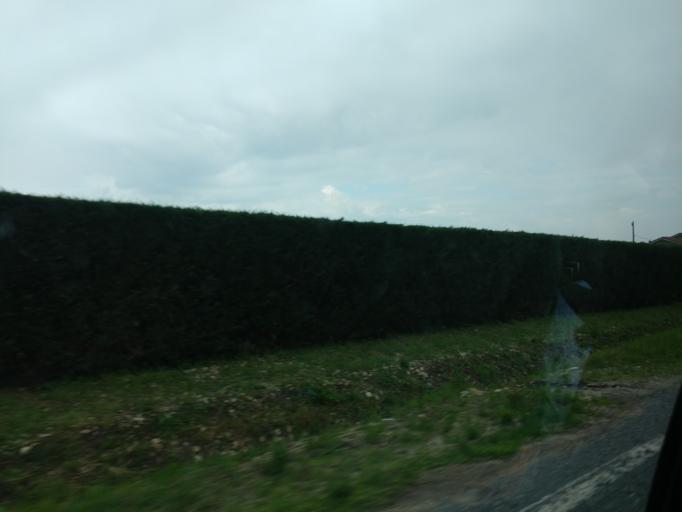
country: IT
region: Piedmont
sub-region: Provincia di Cuneo
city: Revello
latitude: 44.6719
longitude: 7.4017
